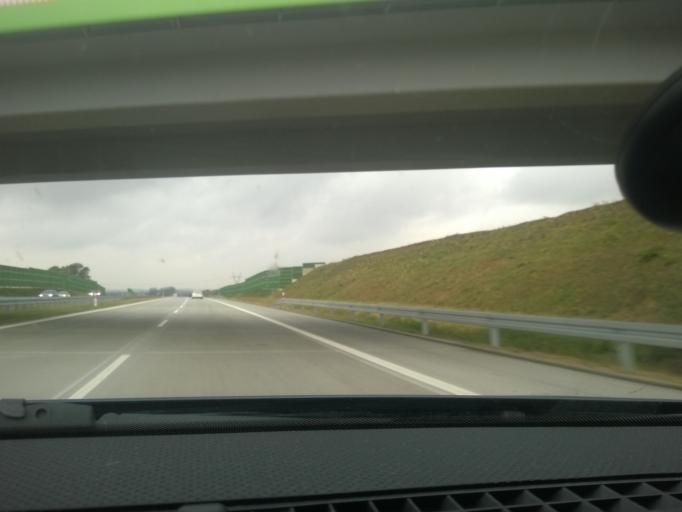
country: PL
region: Lodz Voivodeship
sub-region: Powiat zgierski
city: Strykow
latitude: 51.8558
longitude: 19.6598
